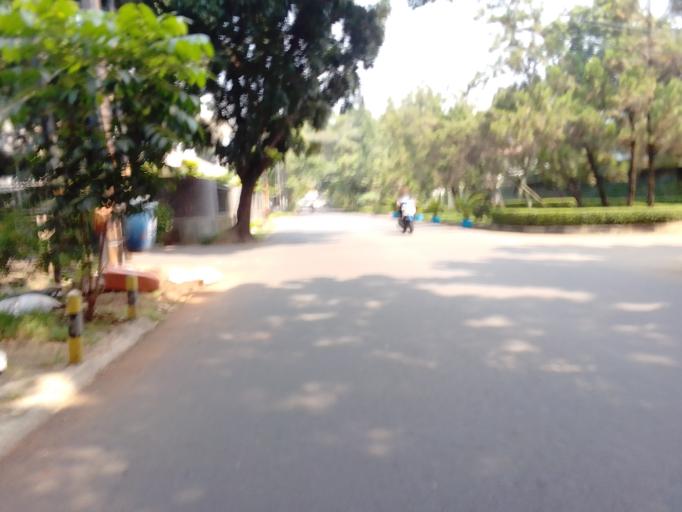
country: ID
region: Jakarta Raya
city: Jakarta
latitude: -6.2256
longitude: 106.7945
